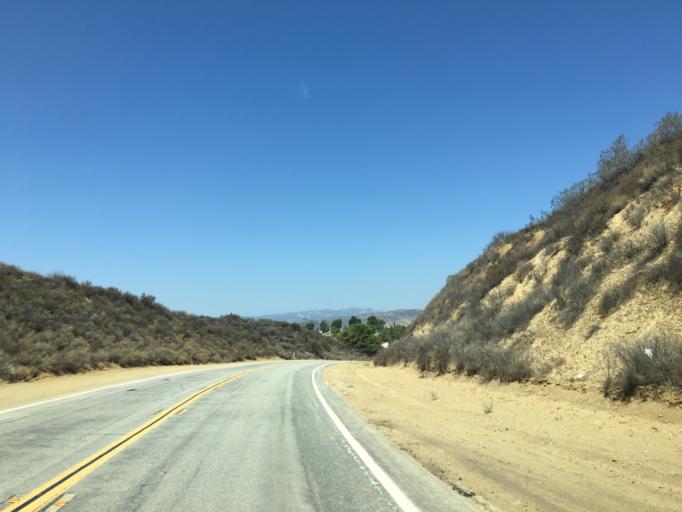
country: US
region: California
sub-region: Los Angeles County
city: Castaic
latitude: 34.5165
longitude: -118.5835
